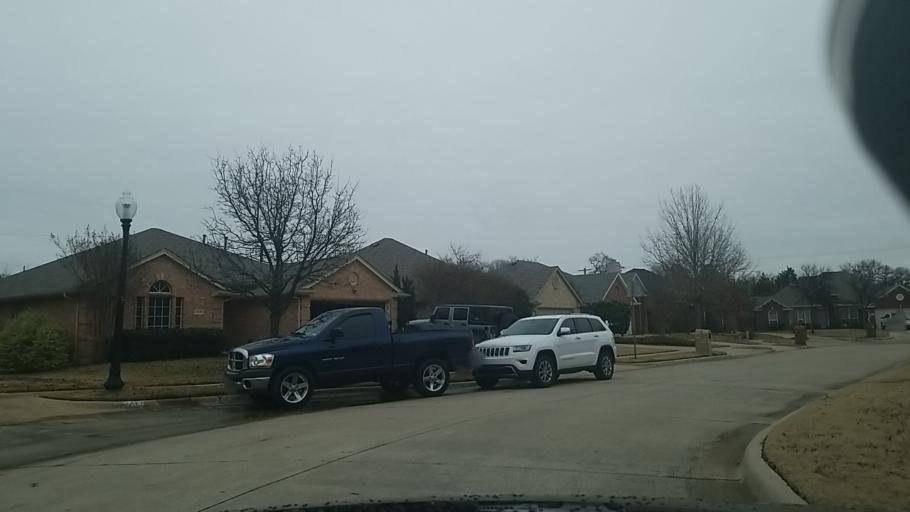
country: US
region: Texas
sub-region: Denton County
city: Corinth
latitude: 33.1553
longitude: -97.0674
